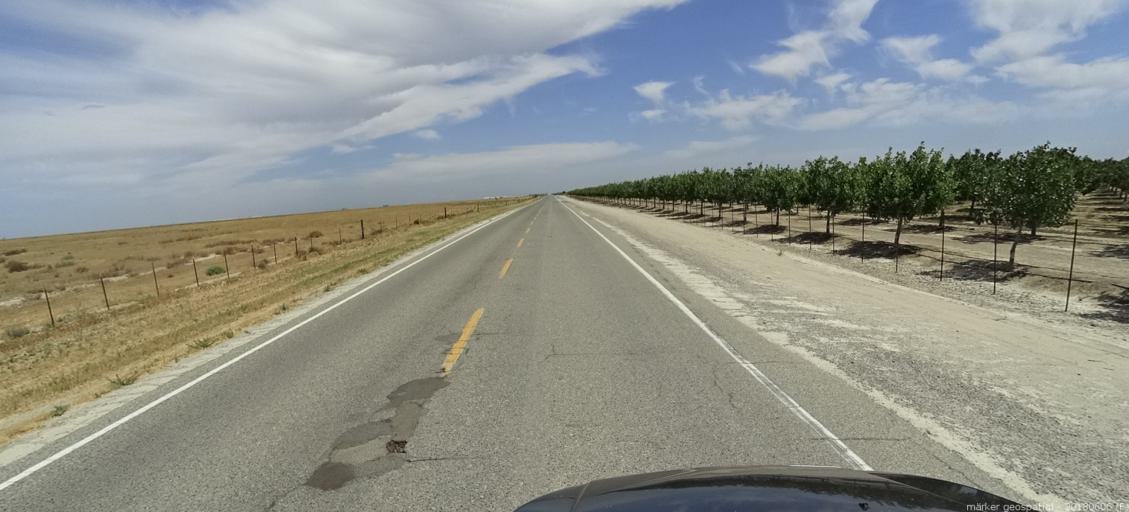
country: US
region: California
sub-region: Fresno County
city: Firebaugh
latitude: 36.8912
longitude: -120.3819
